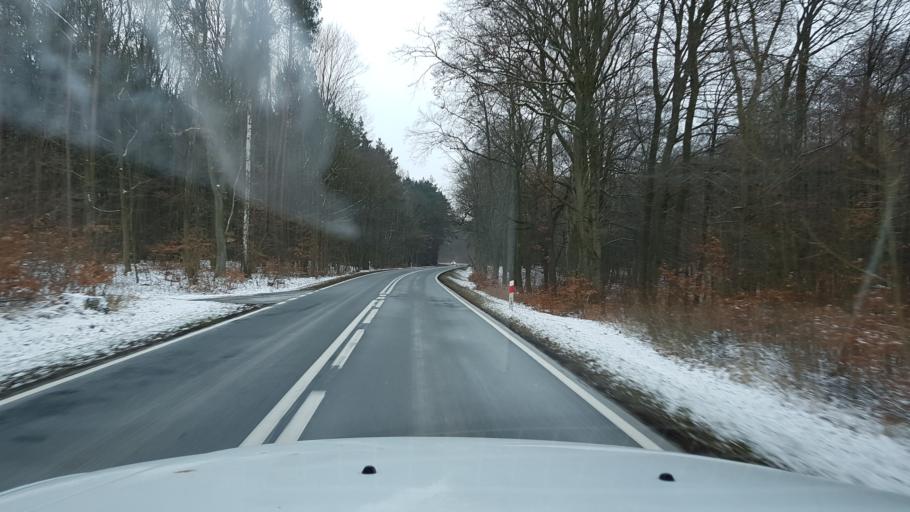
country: PL
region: West Pomeranian Voivodeship
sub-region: Powiat gryfinski
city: Widuchowa
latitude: 53.0829
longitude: 14.4287
